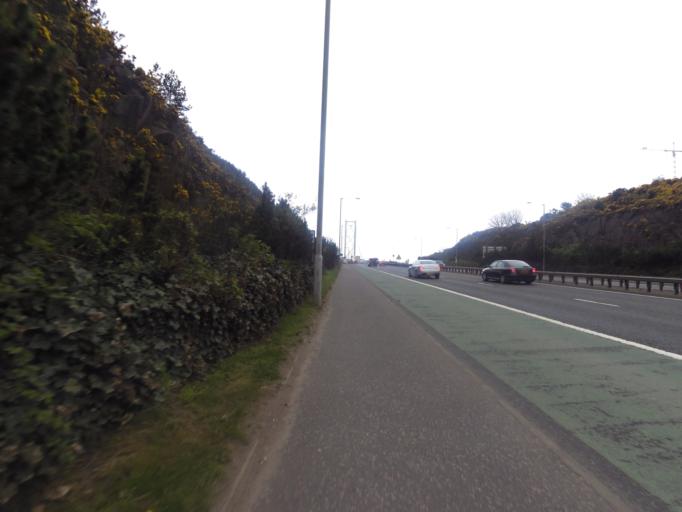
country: GB
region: Scotland
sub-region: Fife
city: North Queensferry
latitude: 56.0134
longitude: -3.4033
